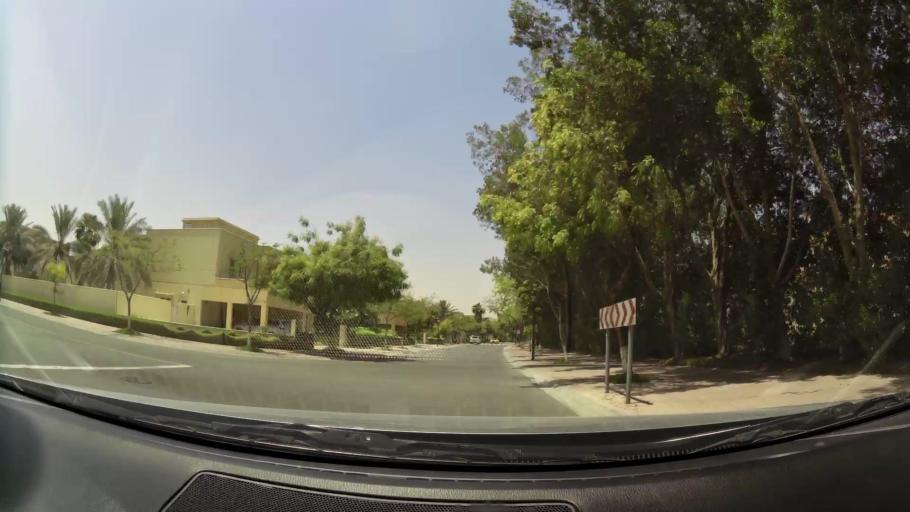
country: AE
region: Dubai
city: Dubai
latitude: 25.0469
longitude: 55.1720
